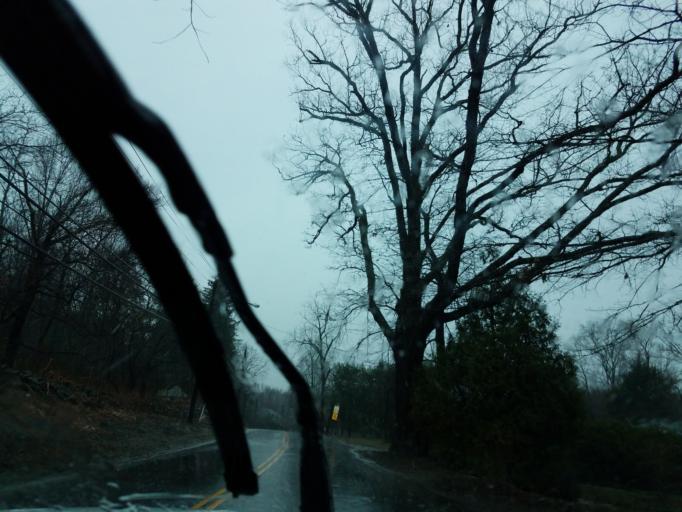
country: US
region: Connecticut
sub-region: New Haven County
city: Waterbury
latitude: 41.5435
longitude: -73.0722
